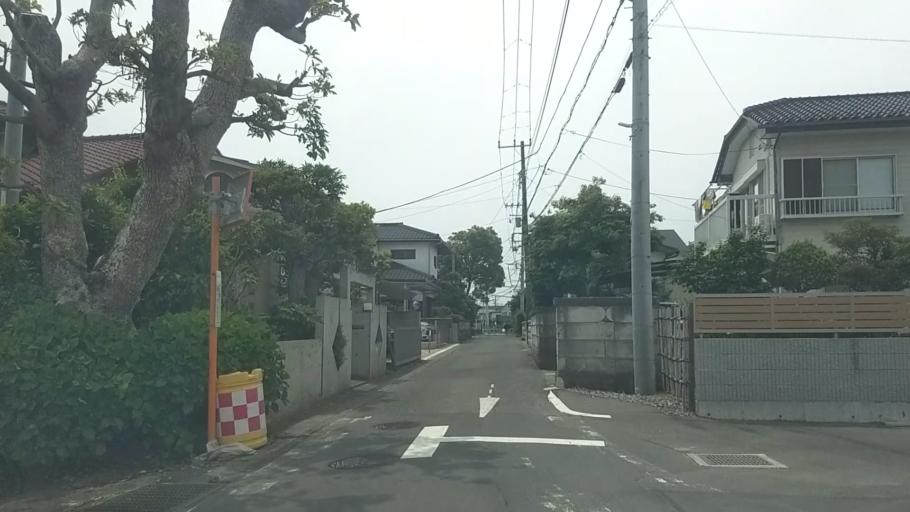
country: JP
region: Kanagawa
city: Chigasaki
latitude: 35.3567
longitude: 139.3961
